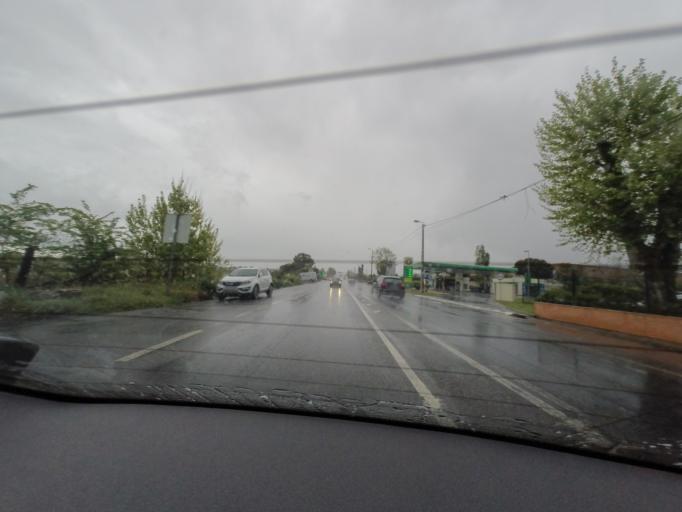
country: PT
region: Lisbon
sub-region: Sintra
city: Sintra
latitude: 38.8242
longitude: -9.3583
